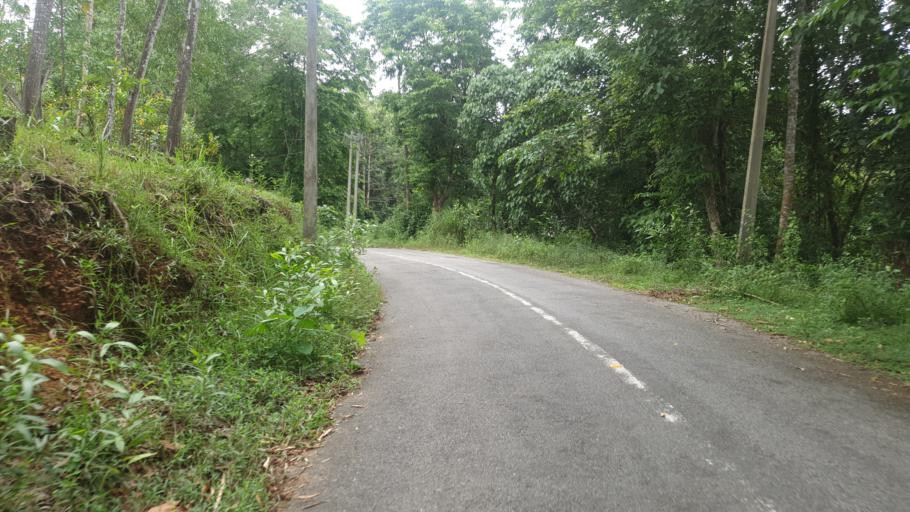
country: IN
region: Kerala
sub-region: Thiruvananthapuram
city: Nedumangad
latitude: 8.6434
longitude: 77.1096
